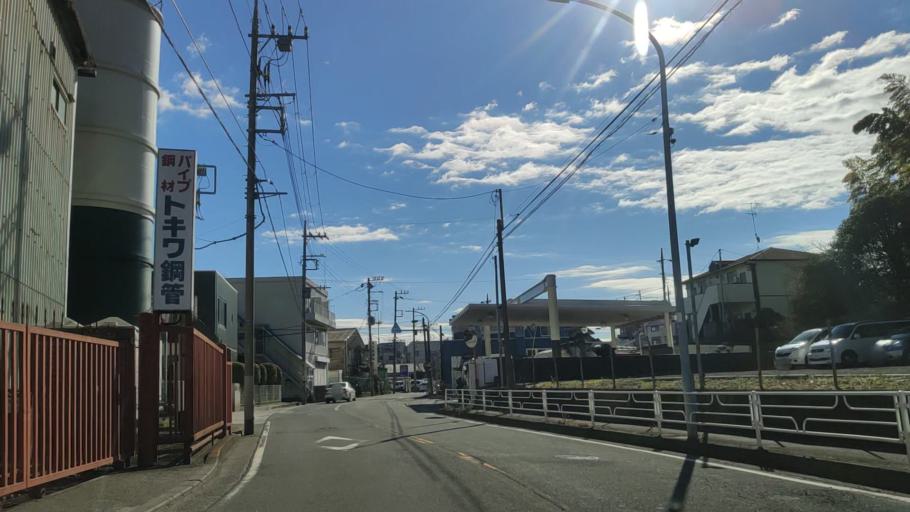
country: JP
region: Kanagawa
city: Yokohama
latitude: 35.4982
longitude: 139.6013
